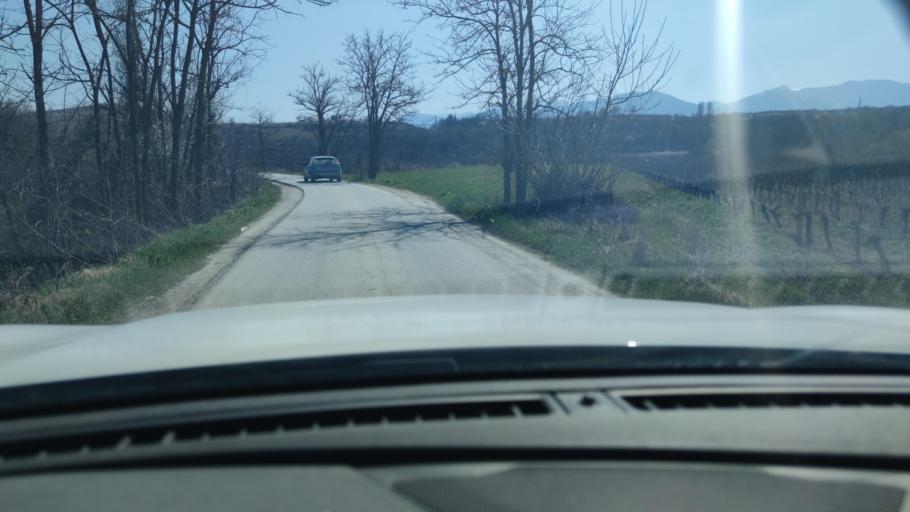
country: MK
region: Rosoman
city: Rosoman
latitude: 41.4748
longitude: 21.9102
